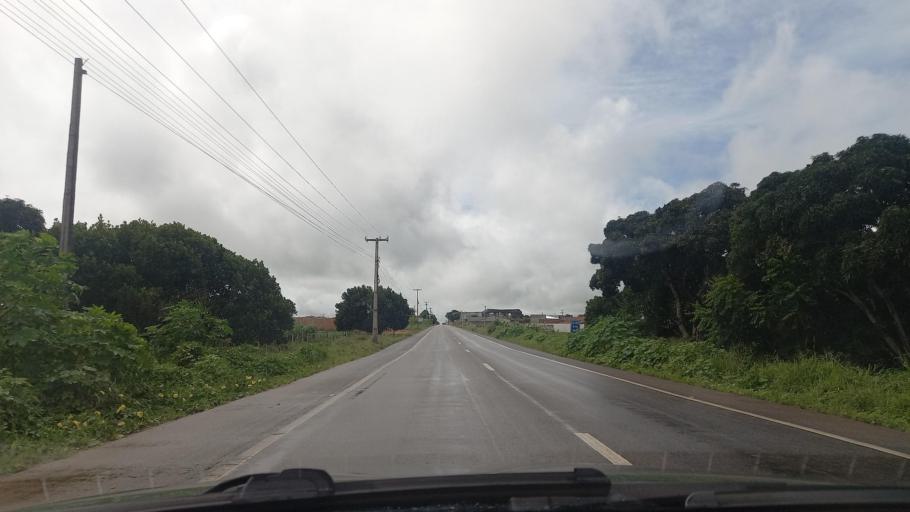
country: BR
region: Alagoas
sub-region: Limoeiro De Anadia
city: Limoeiro de Anadia
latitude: -9.7590
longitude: -36.5645
